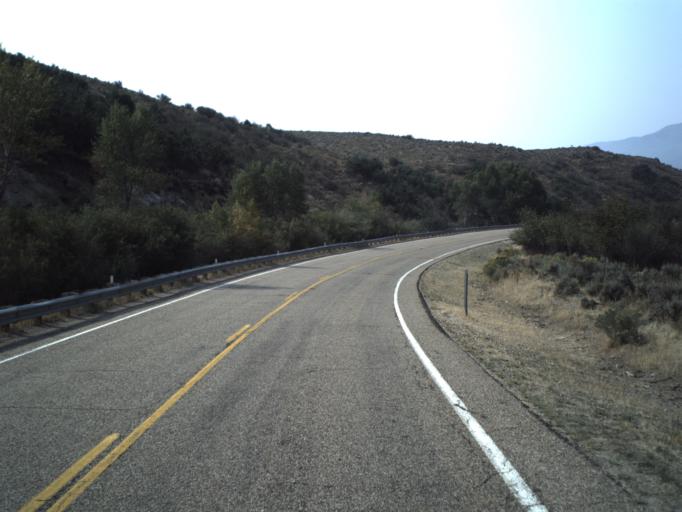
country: US
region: Utah
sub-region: Morgan County
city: Morgan
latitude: 40.9385
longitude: -111.5602
